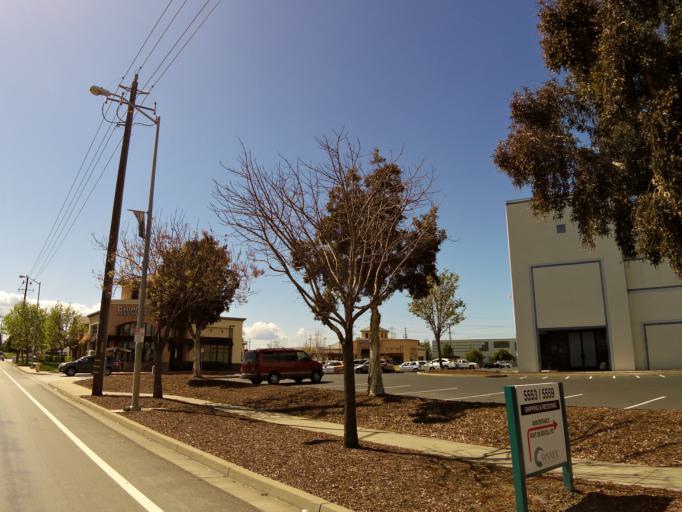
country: US
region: California
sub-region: Alameda County
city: Fremont
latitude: 37.5045
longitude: -121.9749
